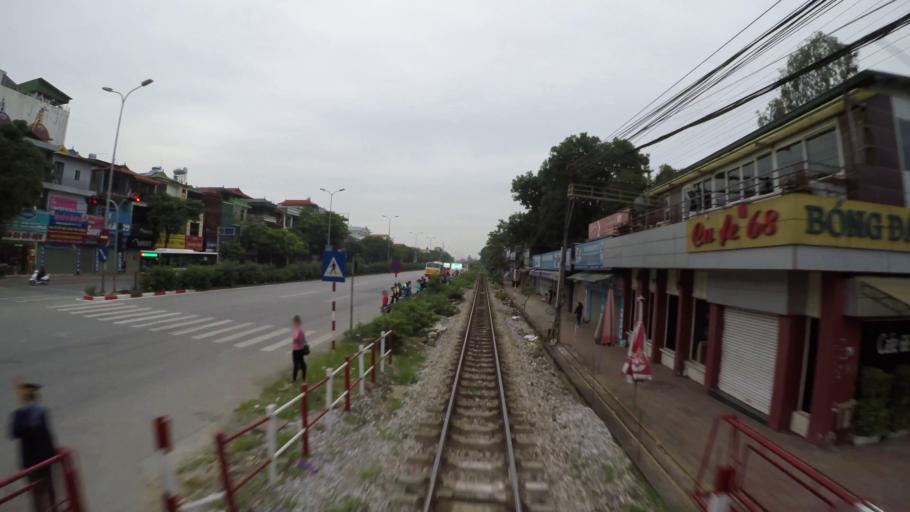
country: VN
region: Ha Noi
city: Trau Quy
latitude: 21.0038
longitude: 105.9619
